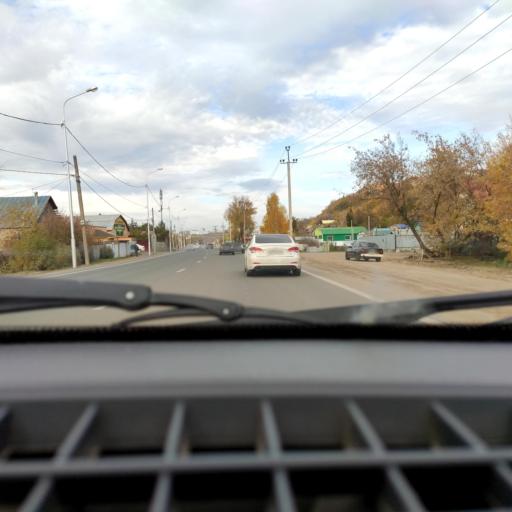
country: RU
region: Bashkortostan
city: Ufa
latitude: 54.6915
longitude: 55.9816
